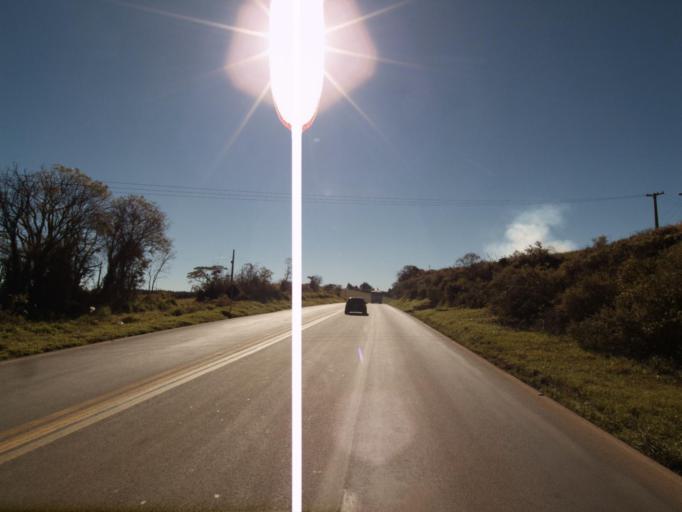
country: BR
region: Santa Catarina
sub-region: Xanxere
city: Xanxere
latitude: -26.9313
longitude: -52.4991
